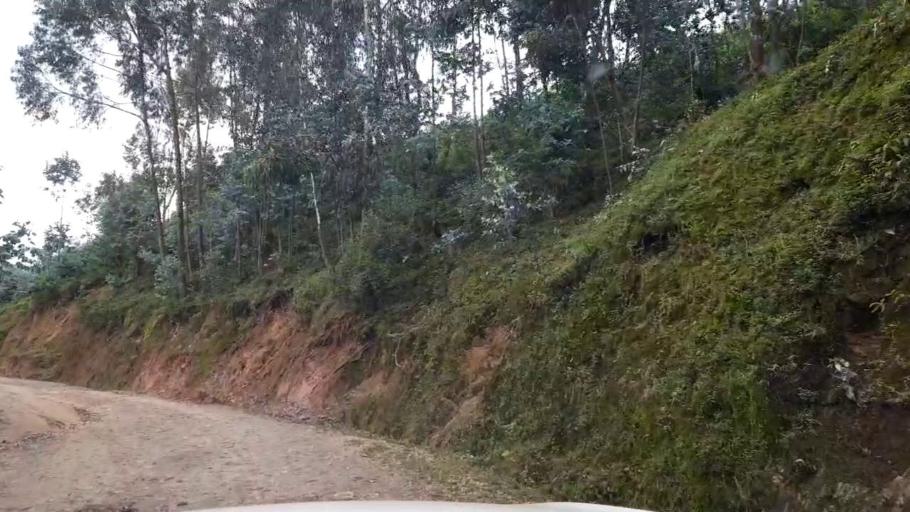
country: RW
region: Western Province
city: Kibuye
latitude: -1.8996
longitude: 29.4541
